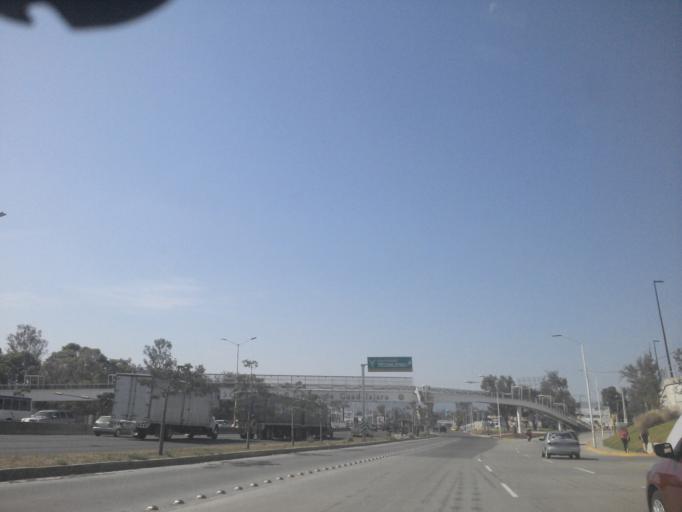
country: MX
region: Jalisco
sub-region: Tlajomulco de Zuniga
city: La Tijera
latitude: 20.6102
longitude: -103.4136
